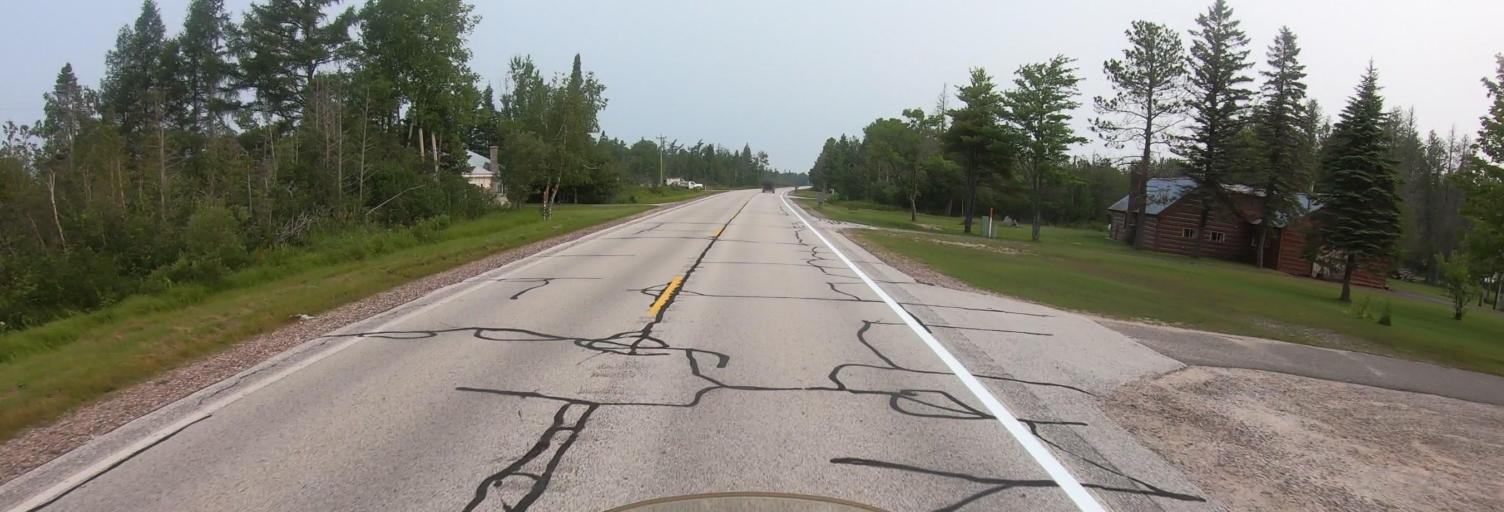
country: US
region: Michigan
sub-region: Luce County
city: Newberry
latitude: 46.5717
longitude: -85.0342
